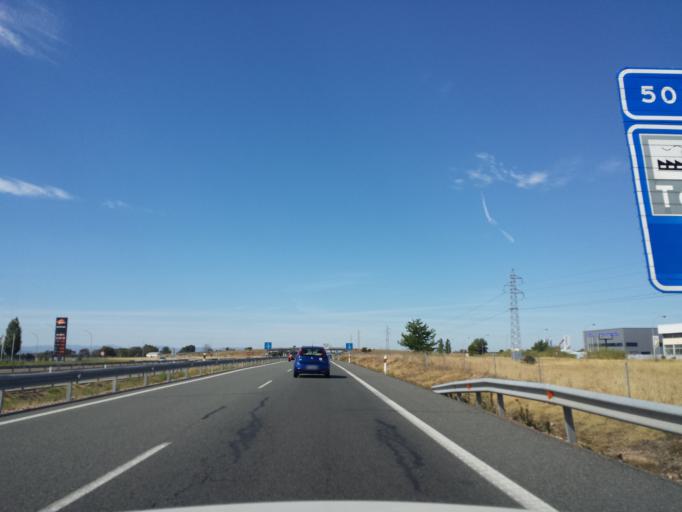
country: ES
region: Castille-La Mancha
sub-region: Province of Toledo
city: Velada
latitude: 39.9538
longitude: -4.9315
